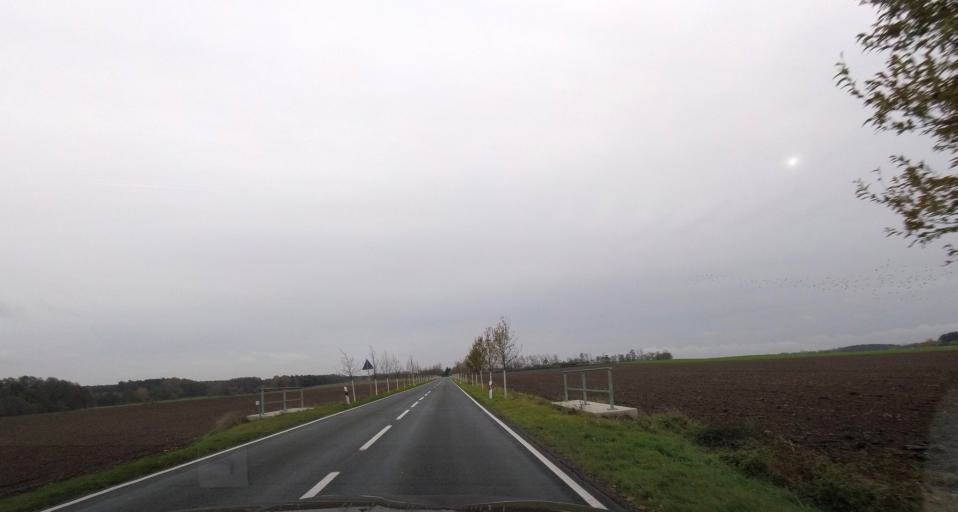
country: DE
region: Brandenburg
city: Niemegk
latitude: 52.0569
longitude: 12.6967
